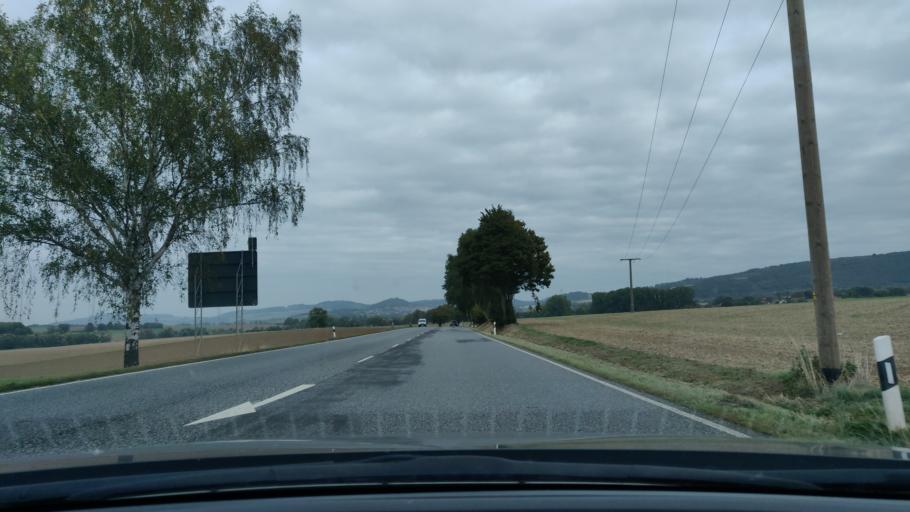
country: DE
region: Hesse
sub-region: Regierungsbezirk Kassel
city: Frielendorf
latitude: 50.9922
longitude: 9.3479
